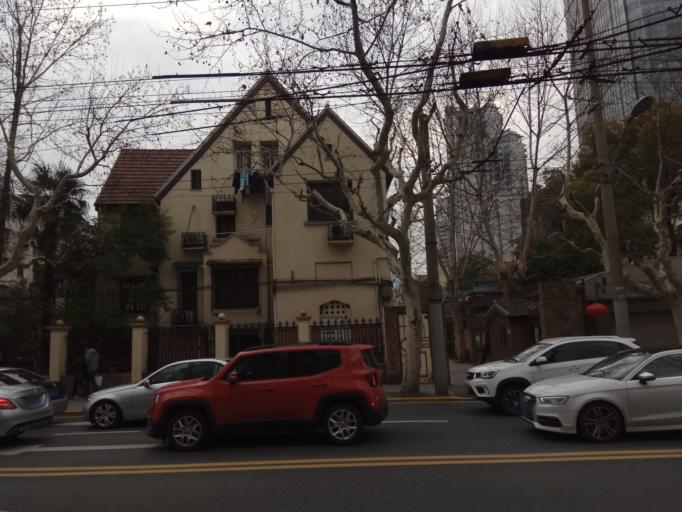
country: CN
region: Shanghai Shi
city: Shanghai
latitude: 31.2169
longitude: 121.4441
